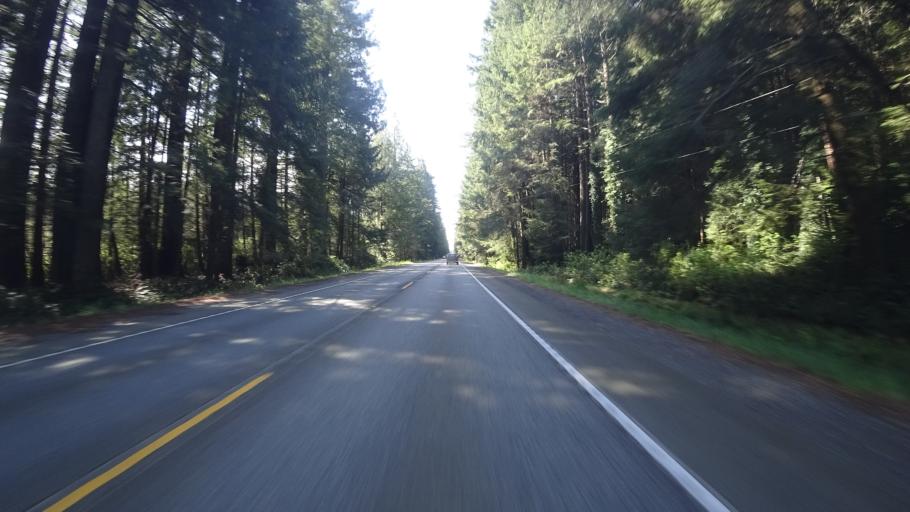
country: US
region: California
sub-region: Del Norte County
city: Bertsch-Oceanview
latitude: 41.8204
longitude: -124.1458
